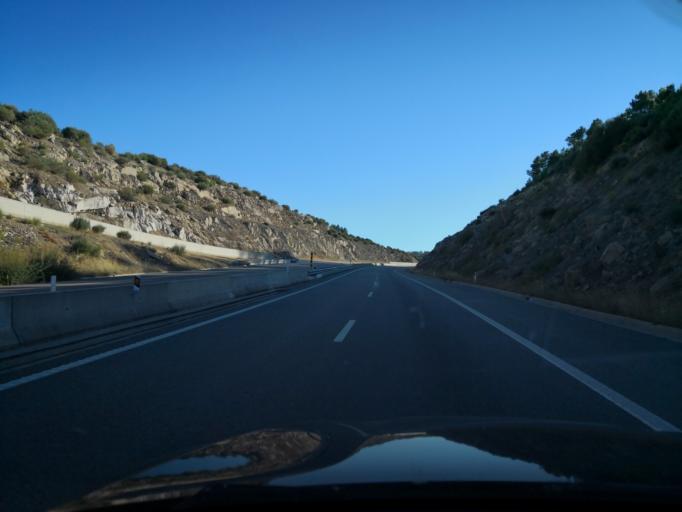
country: PT
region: Vila Real
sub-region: Murca
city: Murca
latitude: 41.3848
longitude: -7.4807
